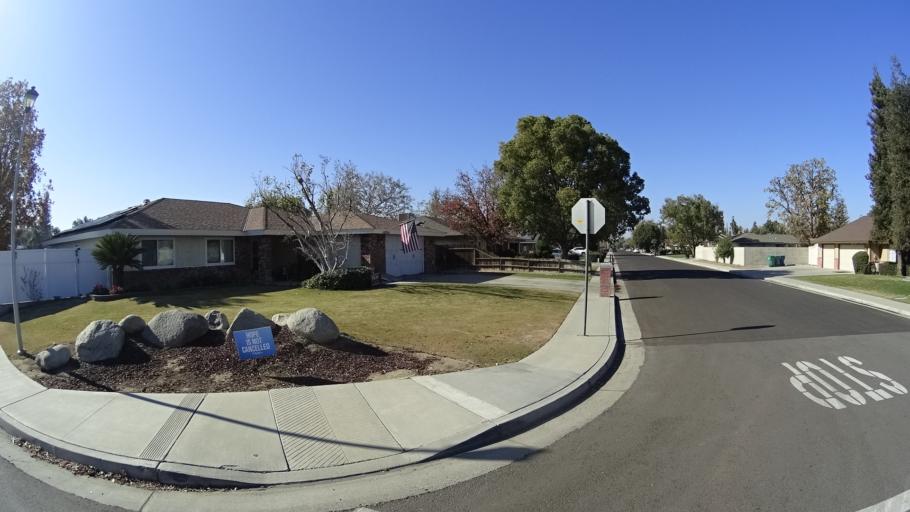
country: US
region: California
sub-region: Kern County
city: Rosedale
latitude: 35.3776
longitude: -119.1281
